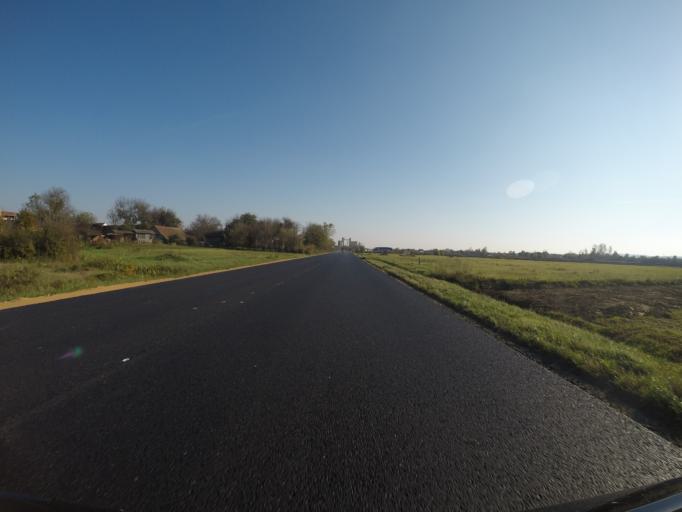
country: HR
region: Koprivnicko-Krizevacka
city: Kalinovac
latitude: 46.0363
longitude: 17.0580
